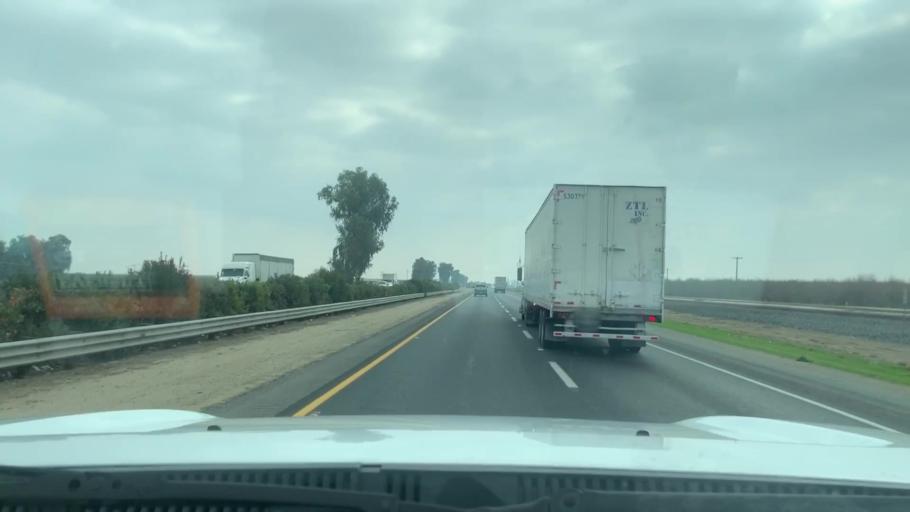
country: US
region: California
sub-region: Tulare County
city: Tipton
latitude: 36.0278
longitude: -119.3073
